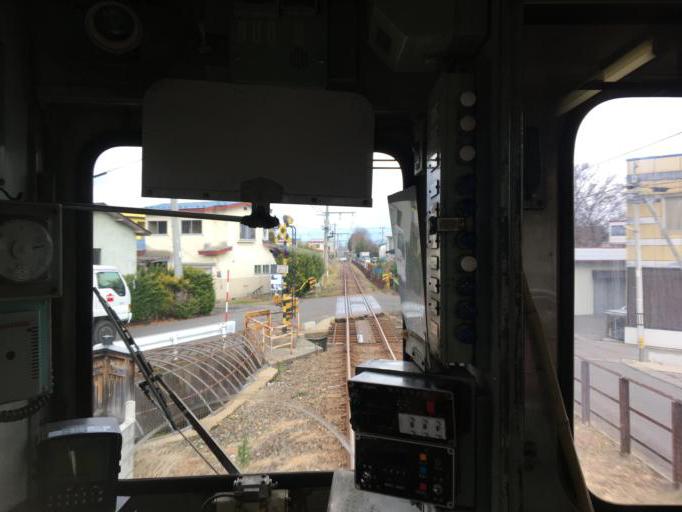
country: JP
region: Aomori
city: Hirosaki
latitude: 40.5749
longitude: 140.4733
